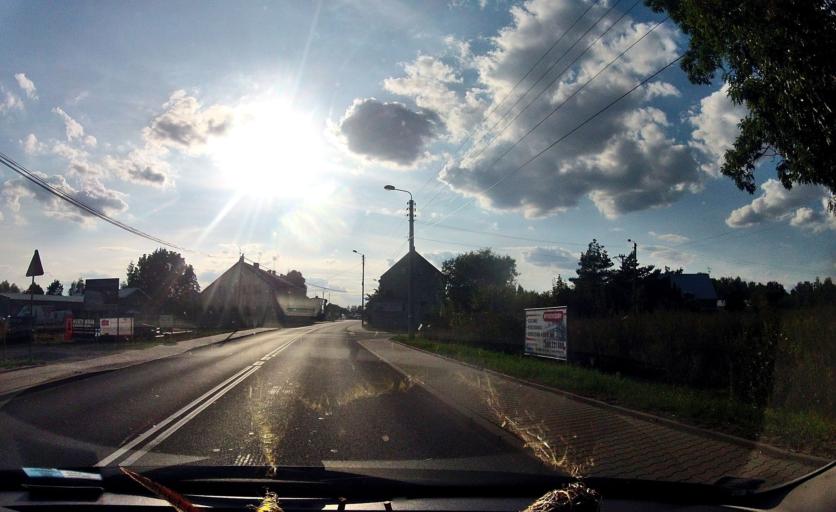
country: PL
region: Opole Voivodeship
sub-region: Powiat oleski
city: Praszka
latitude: 51.0562
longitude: 18.4440
